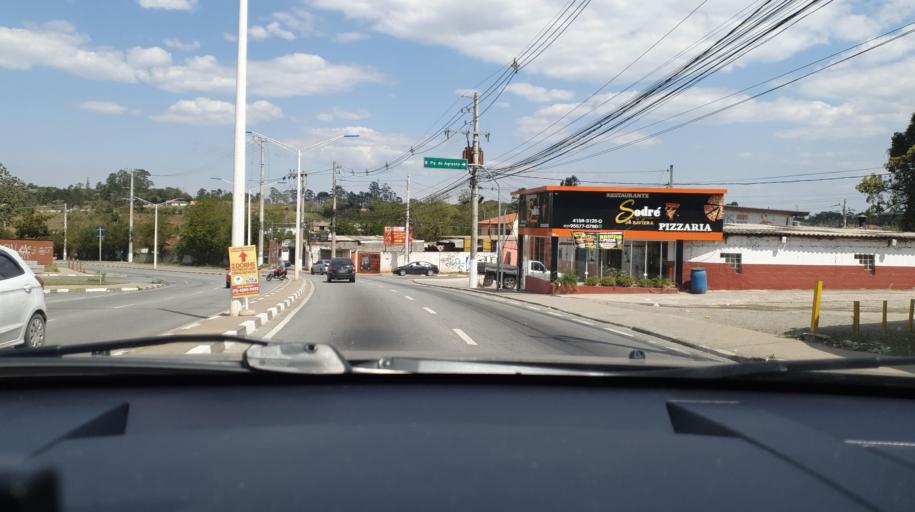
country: BR
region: Sao Paulo
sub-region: Vargem Grande Paulista
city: Vargem Grande Paulista
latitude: -23.6487
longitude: -46.9954
